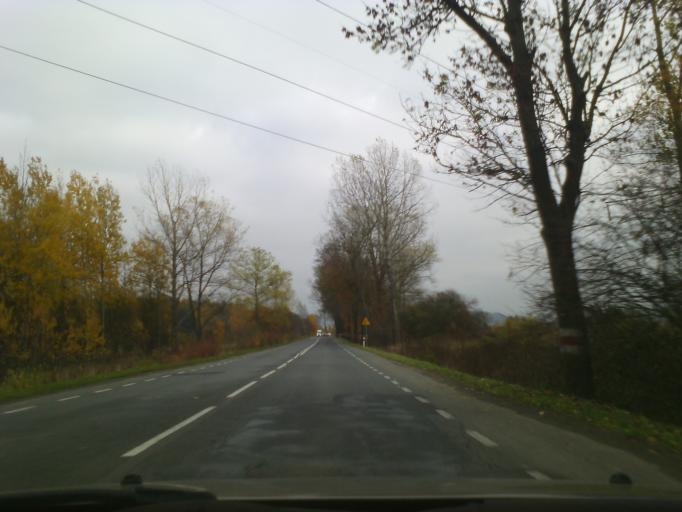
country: PL
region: Lower Silesian Voivodeship
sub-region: Powiat walbrzyski
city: Czarny Bor
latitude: 50.7822
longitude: 16.0967
